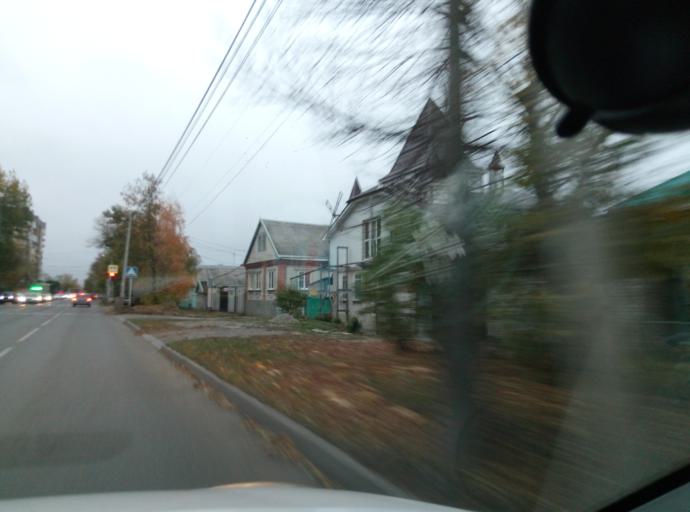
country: RU
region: Stavropol'skiy
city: Yessentukskaya
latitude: 44.0421
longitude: 42.8770
